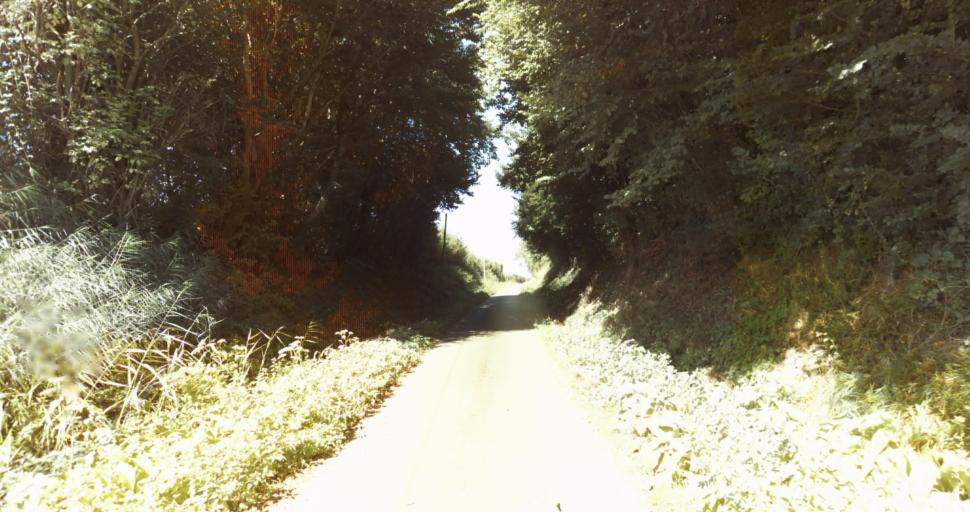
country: FR
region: Lower Normandy
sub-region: Departement de l'Orne
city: Gace
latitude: 48.7603
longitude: 0.2688
